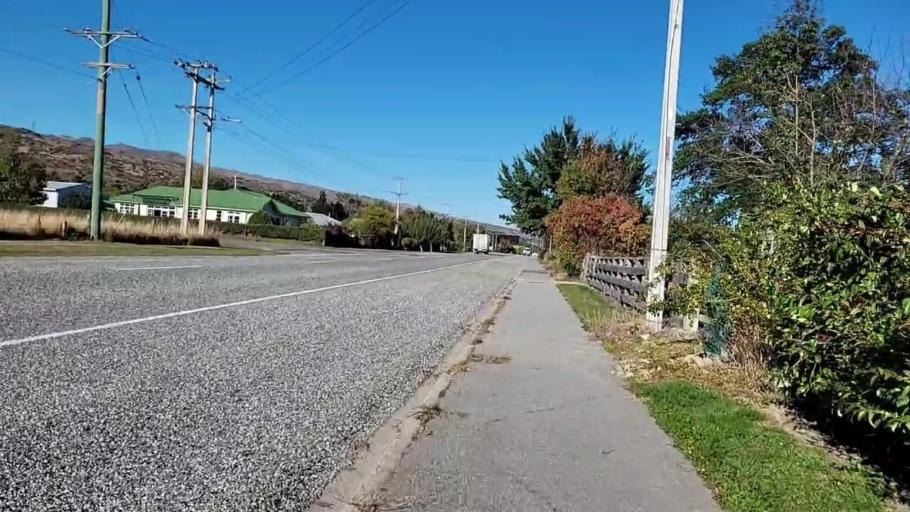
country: NZ
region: Otago
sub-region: Queenstown-Lakes District
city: Wanaka
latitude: -45.0052
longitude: 169.9147
